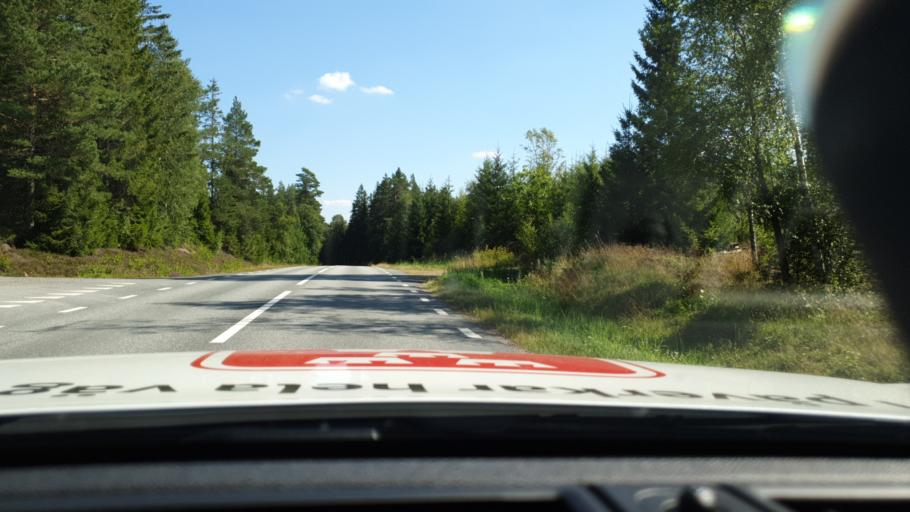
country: SE
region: Joenkoeping
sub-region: Aneby Kommun
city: Hestra
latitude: 57.8995
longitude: 14.5666
